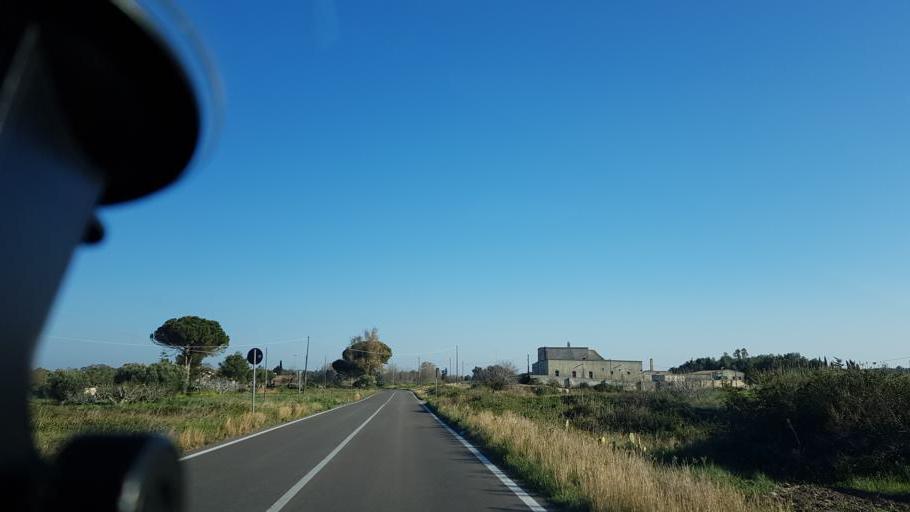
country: IT
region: Apulia
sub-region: Provincia di Lecce
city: Merine
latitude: 40.4139
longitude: 18.2535
